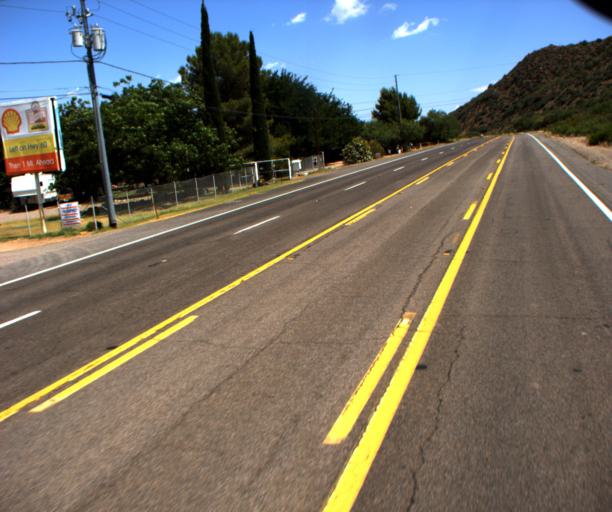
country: US
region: Arizona
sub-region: Gila County
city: Claypool
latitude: 33.4637
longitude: -110.8508
